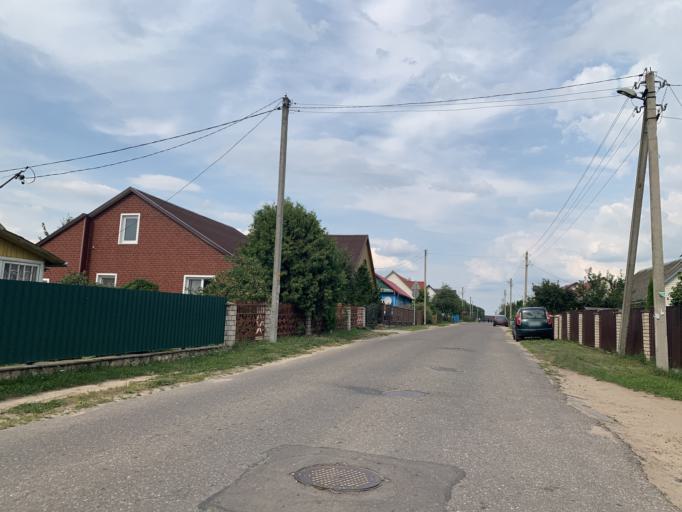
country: BY
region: Minsk
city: Nyasvizh
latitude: 53.2074
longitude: 26.6854
